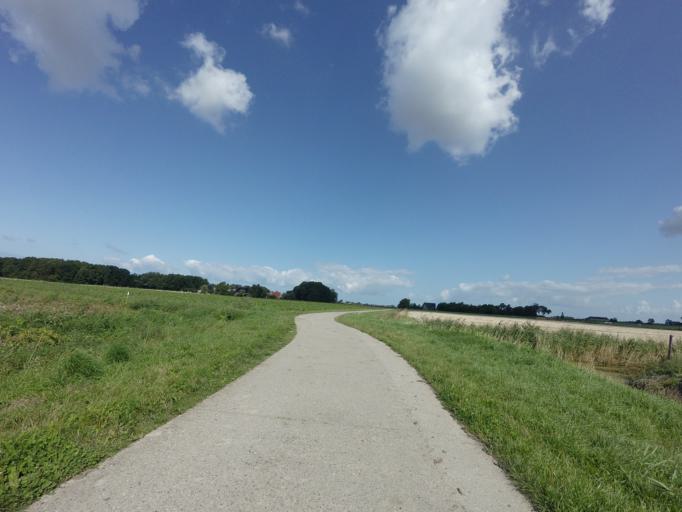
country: NL
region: Friesland
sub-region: Gemeente Het Bildt
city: Sint Jacobiparochie
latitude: 53.2699
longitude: 5.6160
